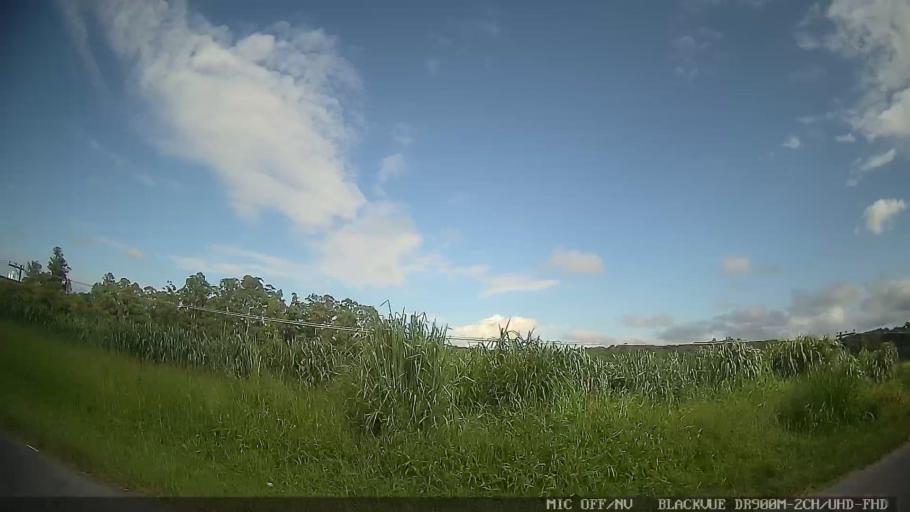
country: BR
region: Sao Paulo
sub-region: Jarinu
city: Jarinu
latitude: -23.0620
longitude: -46.6825
